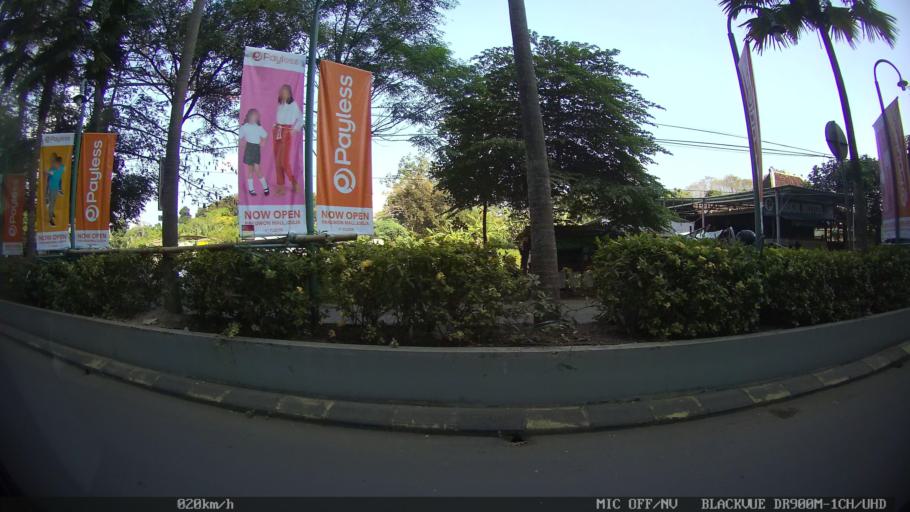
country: ID
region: Daerah Istimewa Yogyakarta
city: Depok
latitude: -7.7590
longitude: 110.3986
